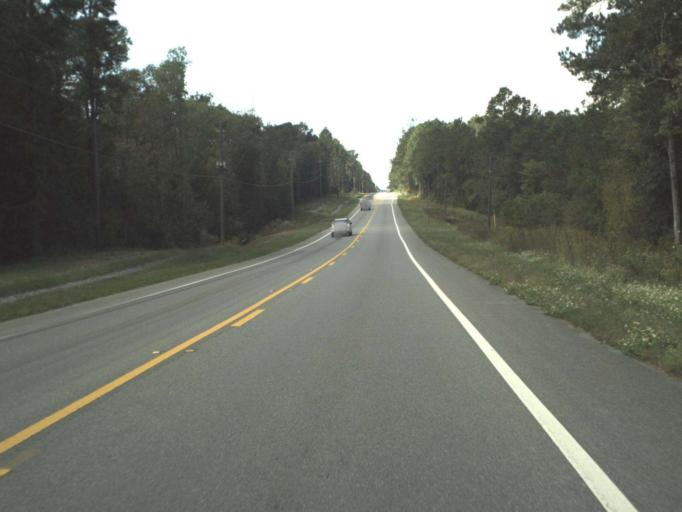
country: US
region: Florida
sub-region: Walton County
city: Freeport
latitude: 30.4776
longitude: -86.0498
